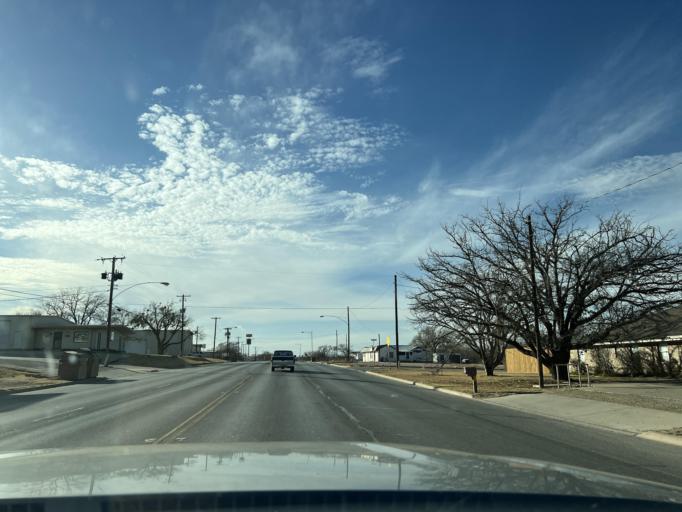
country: US
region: Texas
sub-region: Scurry County
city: Snyder
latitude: 32.7173
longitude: -100.9286
